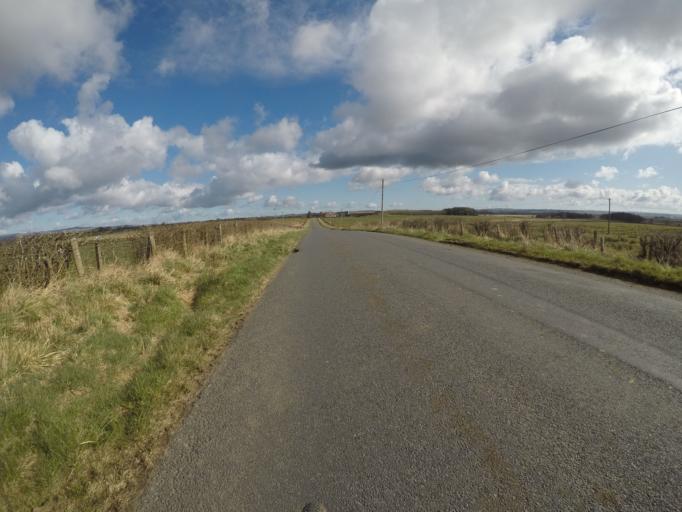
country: GB
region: Scotland
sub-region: North Ayrshire
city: Kilwinning
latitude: 55.6841
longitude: -4.6498
